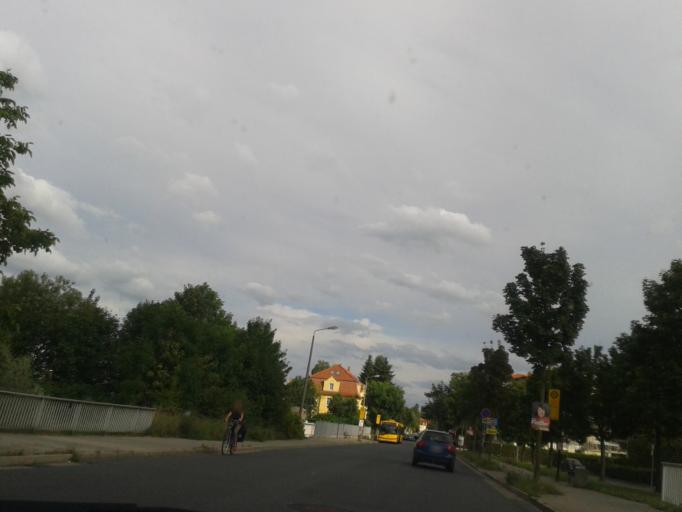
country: DE
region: Saxony
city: Dresden
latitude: 51.0190
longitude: 13.7580
